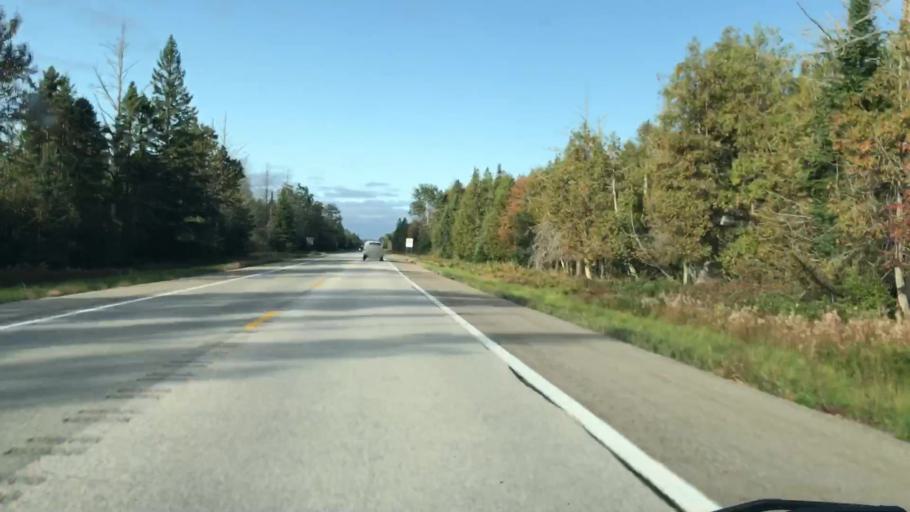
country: US
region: Michigan
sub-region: Luce County
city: Newberry
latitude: 46.3274
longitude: -85.1624
